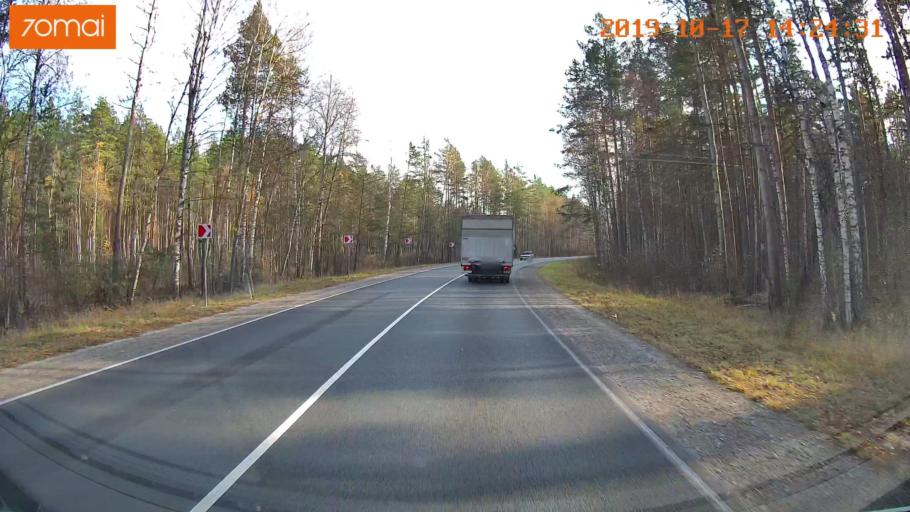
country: RU
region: Moskovskaya
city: Radovitskiy
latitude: 55.0088
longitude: 39.9690
